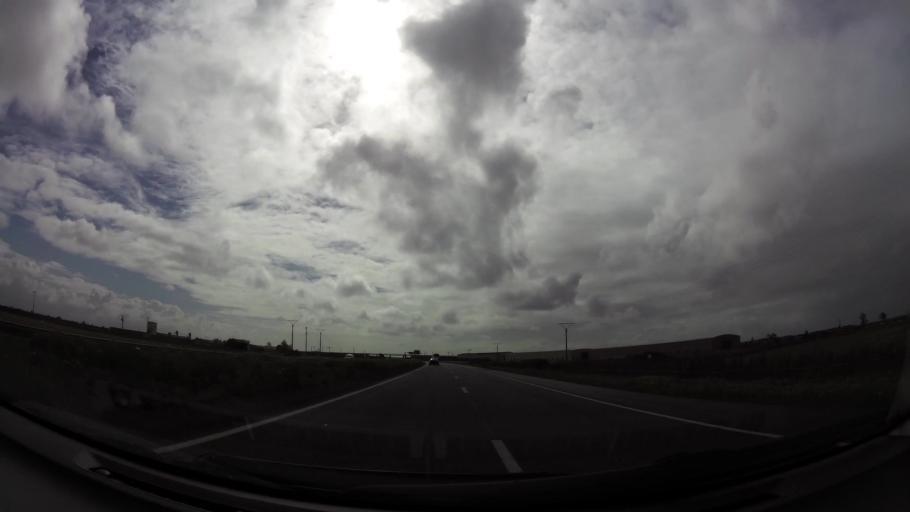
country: MA
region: Grand Casablanca
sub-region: Nouaceur
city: Dar Bouazza
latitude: 33.3530
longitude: -7.9877
